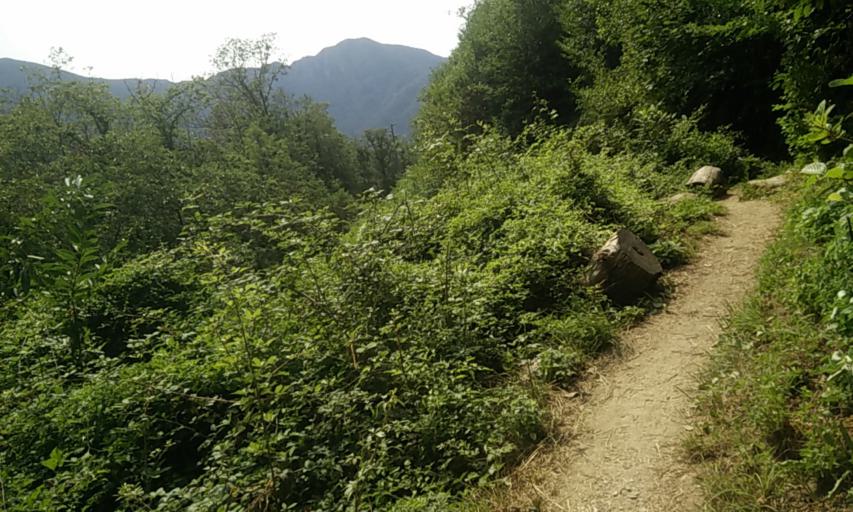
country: IT
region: Tuscany
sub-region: Provincia di Lucca
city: Pontestazzemese
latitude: 43.9949
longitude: 10.3290
